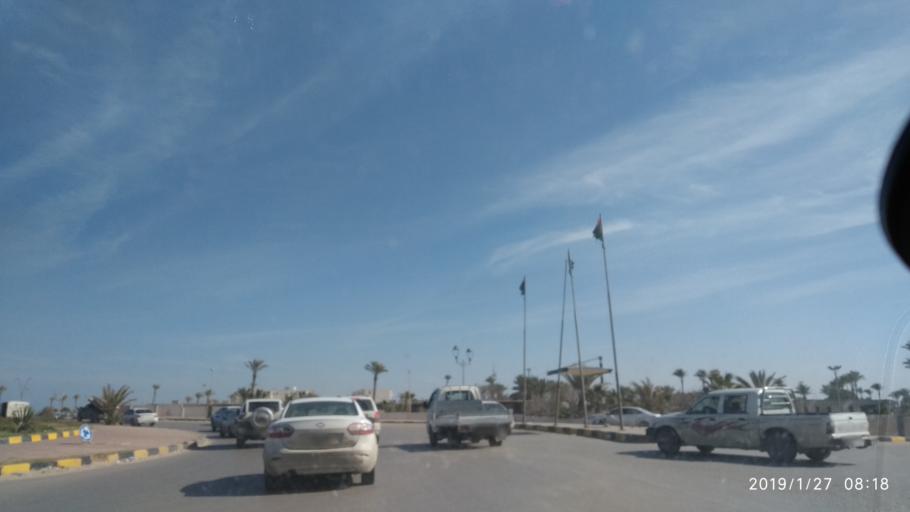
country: LY
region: Tripoli
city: Tripoli
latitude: 32.9067
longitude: 13.2672
